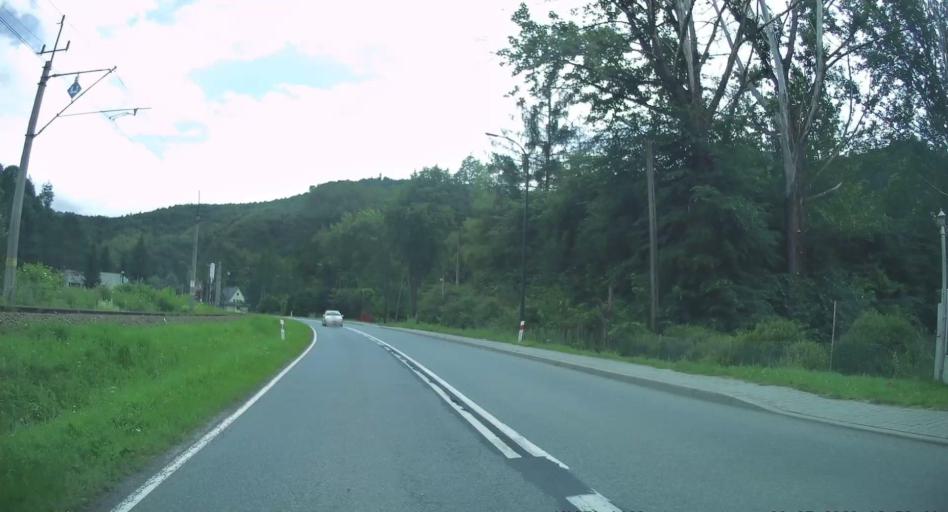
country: PL
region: Lesser Poland Voivodeship
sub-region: Powiat nowosadecki
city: Piwniczna-Zdroj
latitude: 49.3631
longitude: 20.7832
